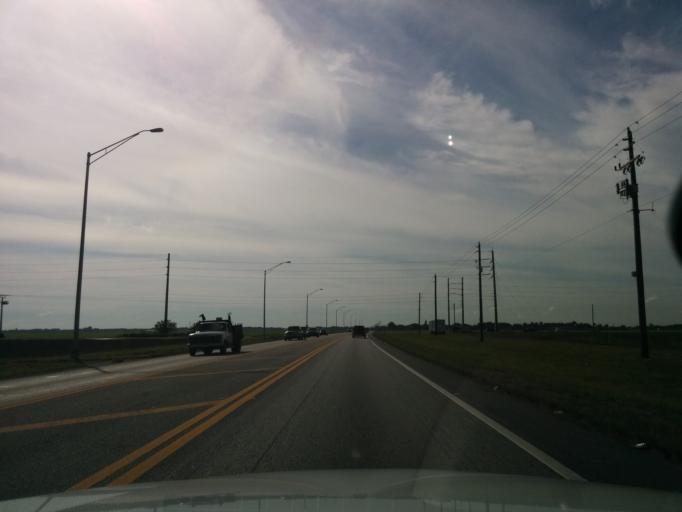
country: US
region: Florida
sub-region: Miami-Dade County
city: The Hammocks
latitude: 25.6401
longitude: -80.4799
